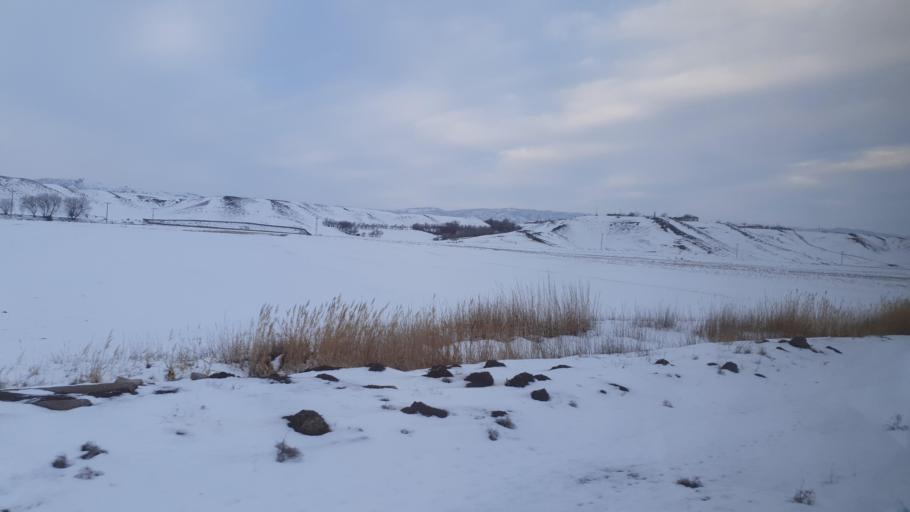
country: TR
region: Kirsehir
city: Mecidiye
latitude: 39.6862
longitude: 34.3975
